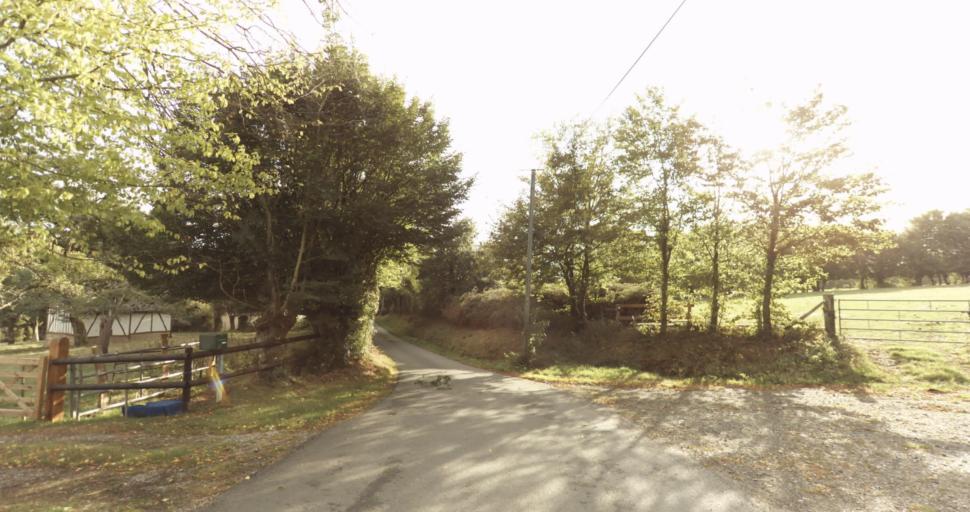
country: FR
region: Lower Normandy
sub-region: Departement de l'Orne
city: Sainte-Gauburge-Sainte-Colombe
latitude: 48.7172
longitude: 0.4104
